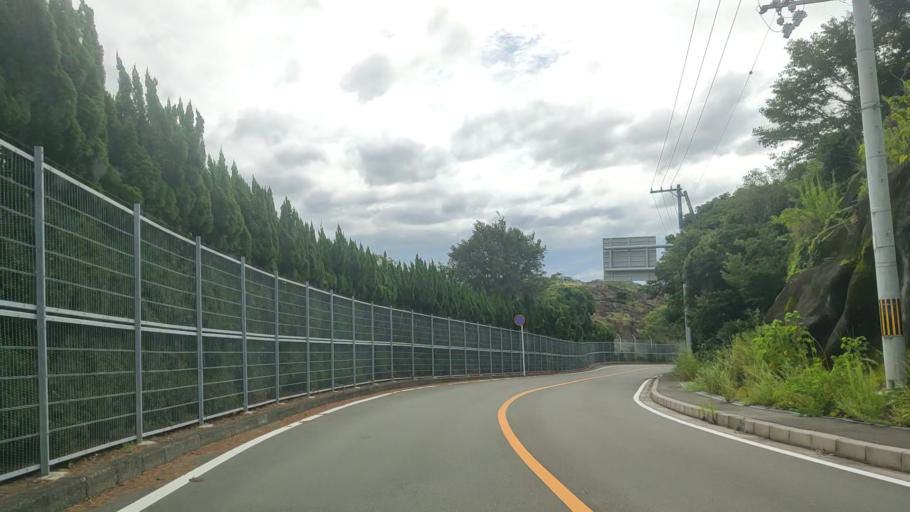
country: JP
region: Wakayama
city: Tanabe
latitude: 33.6654
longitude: 135.3674
